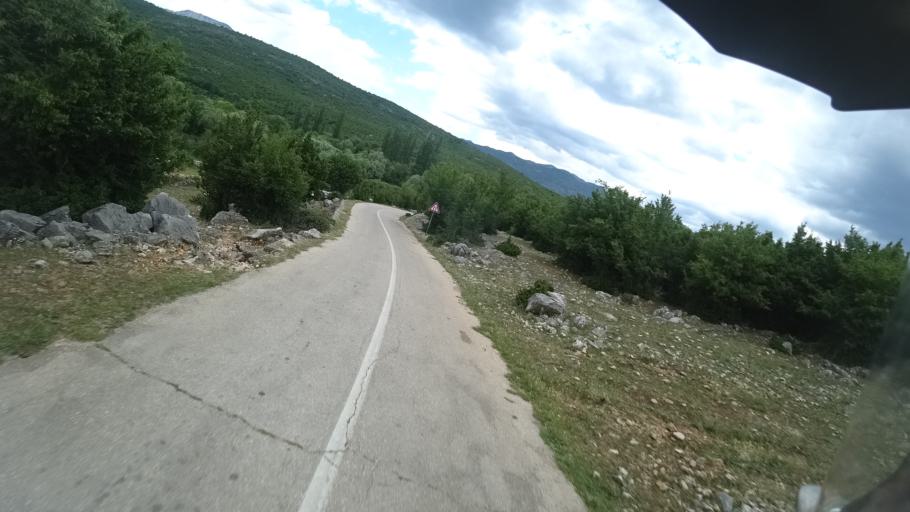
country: HR
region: Zadarska
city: Gracac
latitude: 44.1889
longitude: 15.8869
